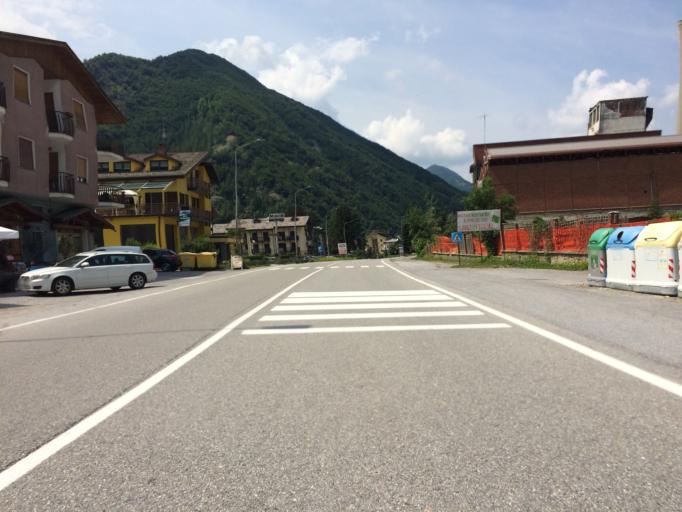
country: IT
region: Piedmont
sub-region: Provincia di Cuneo
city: Vernante
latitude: 44.2413
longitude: 7.5375
